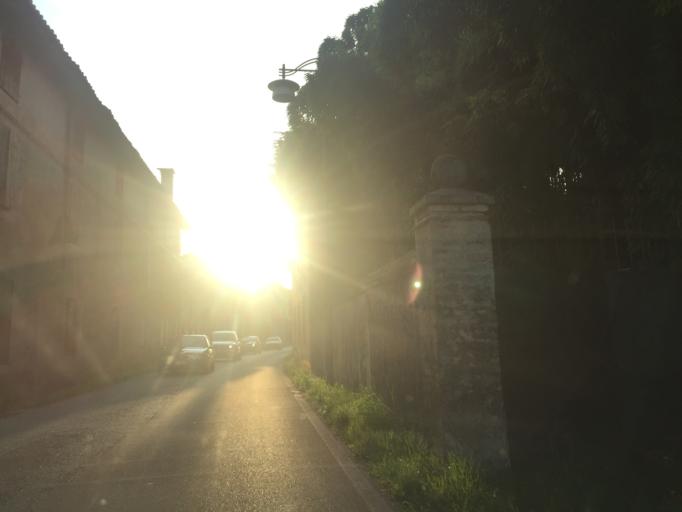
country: IT
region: Friuli Venezia Giulia
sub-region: Provincia di Pordenone
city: Cavolano-Schiavoi
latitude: 45.9365
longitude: 12.4750
